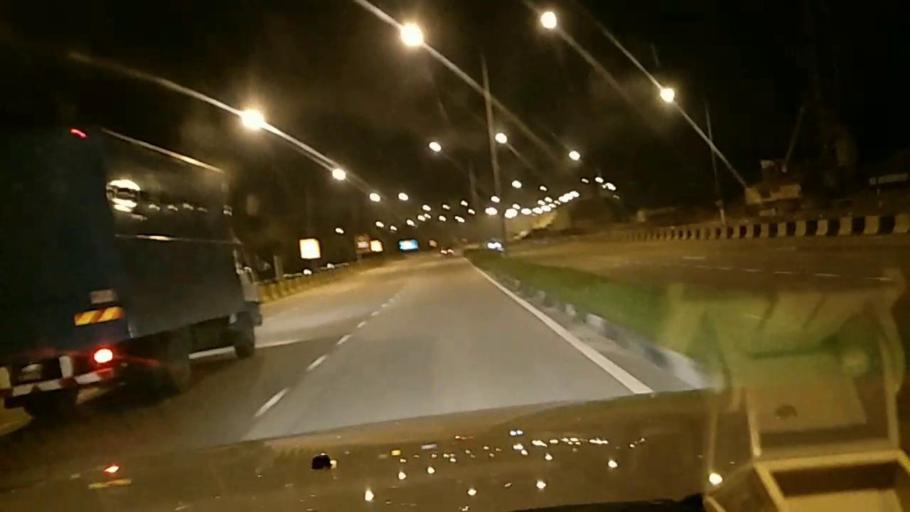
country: MY
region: Selangor
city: Kampung Baru Subang
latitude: 3.1344
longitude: 101.4966
